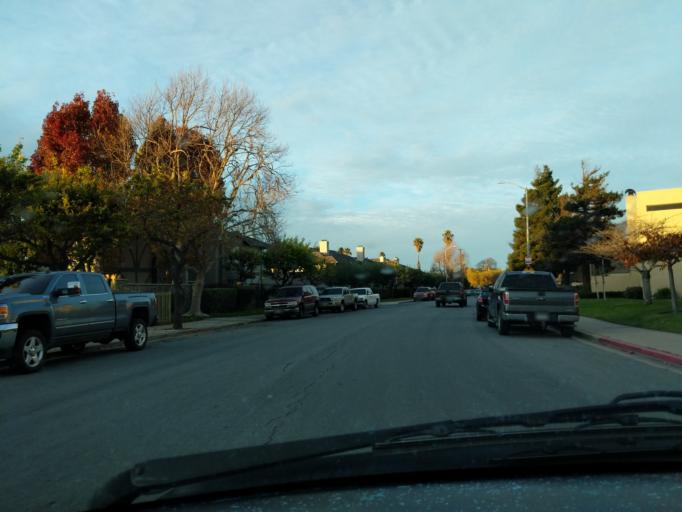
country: US
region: California
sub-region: Monterey County
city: Salinas
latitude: 36.6598
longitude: -121.6614
